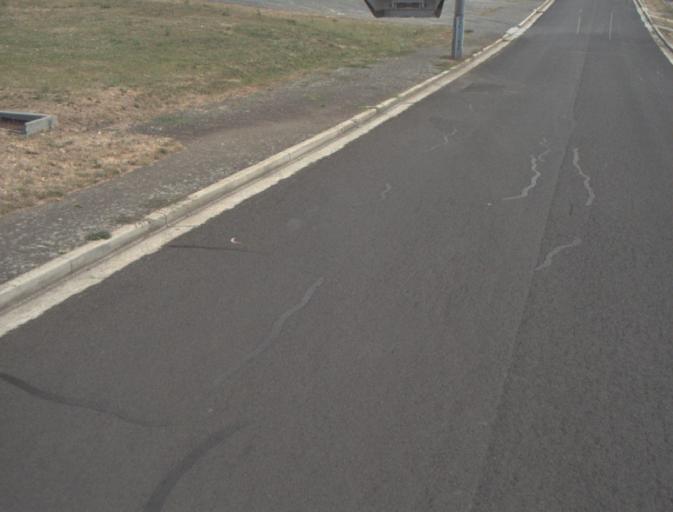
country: AU
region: Tasmania
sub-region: Launceston
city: Newstead
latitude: -41.4578
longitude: 147.2020
